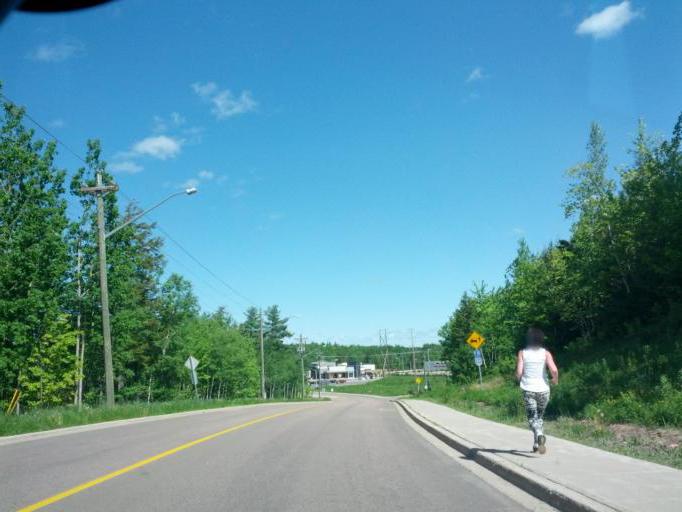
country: CA
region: New Brunswick
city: Moncton
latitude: 46.1219
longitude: -64.8328
